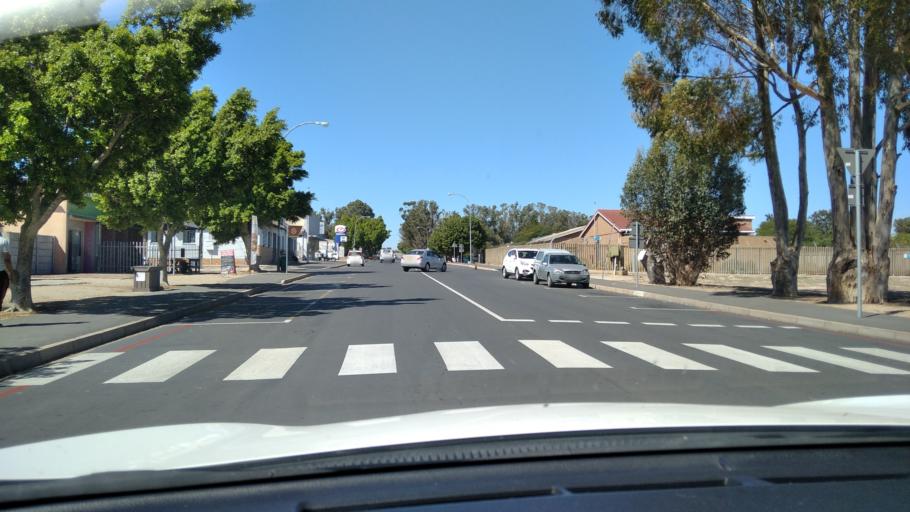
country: ZA
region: Western Cape
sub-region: West Coast District Municipality
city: Moorreesburg
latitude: -33.0629
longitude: 18.3501
